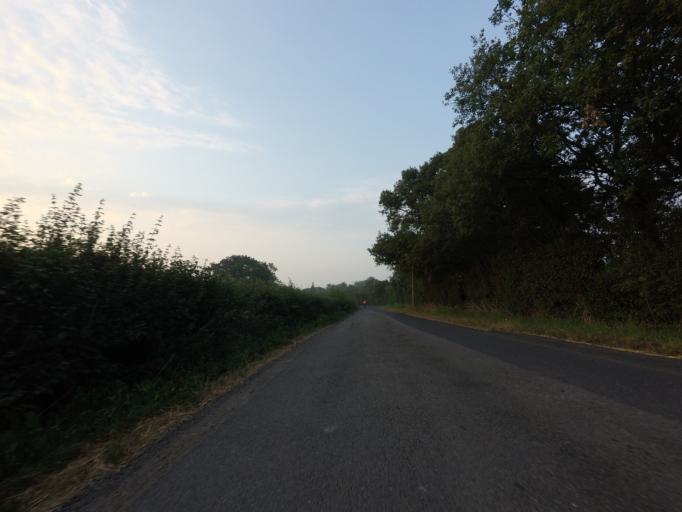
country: GB
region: England
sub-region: Kent
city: Lenham
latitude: 51.1916
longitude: 0.7050
